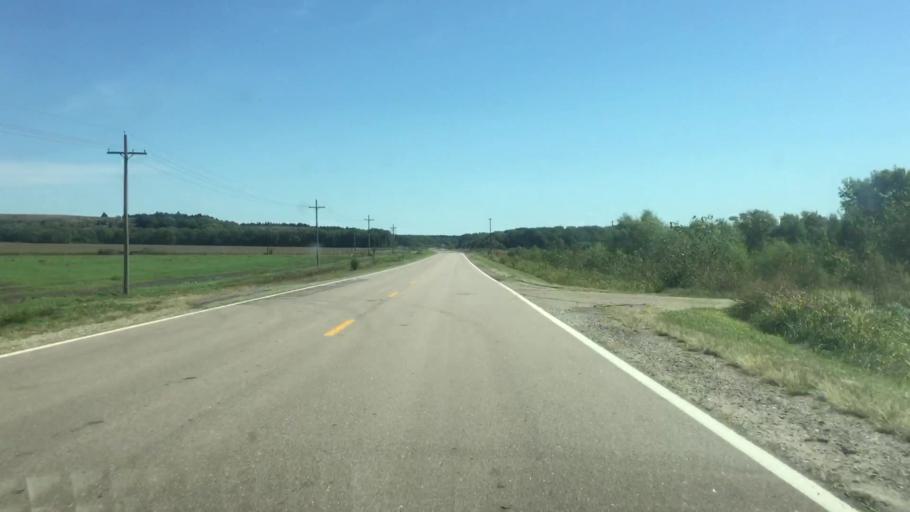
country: US
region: Nebraska
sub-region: Jefferson County
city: Fairbury
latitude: 40.0780
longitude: -97.0897
